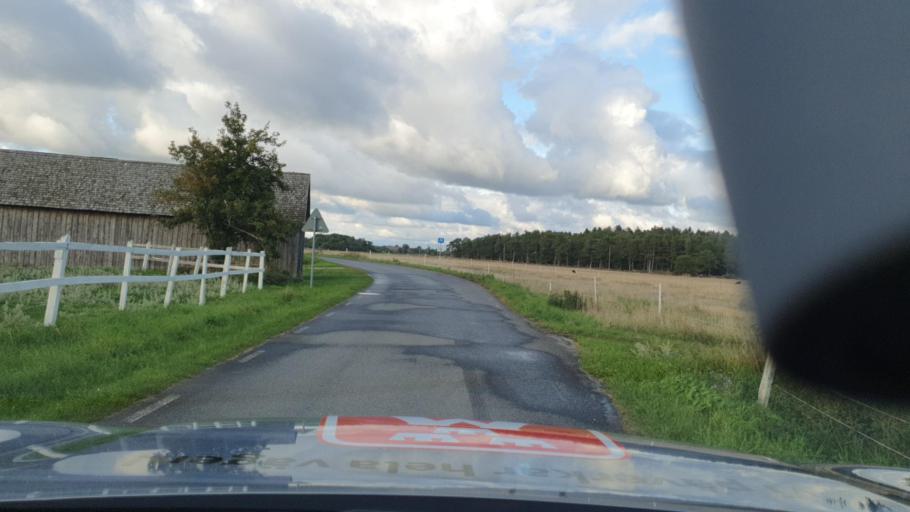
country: SE
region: Gotland
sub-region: Gotland
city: Hemse
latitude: 57.2168
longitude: 18.2344
